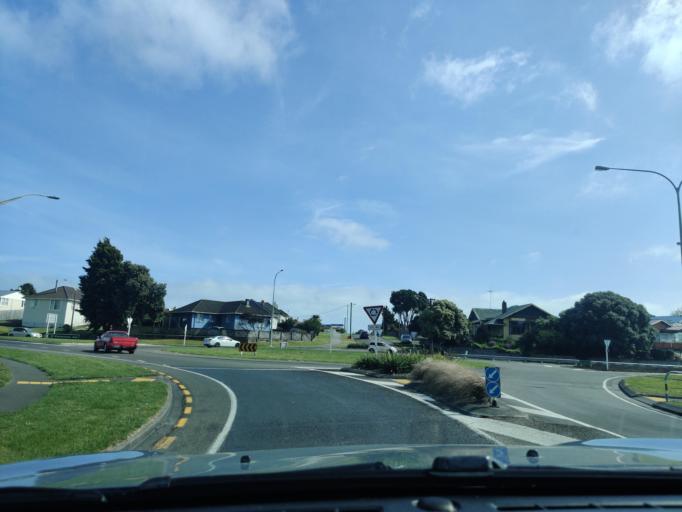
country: NZ
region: Manawatu-Wanganui
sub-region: Wanganui District
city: Wanganui
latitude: -39.9326
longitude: 175.0290
